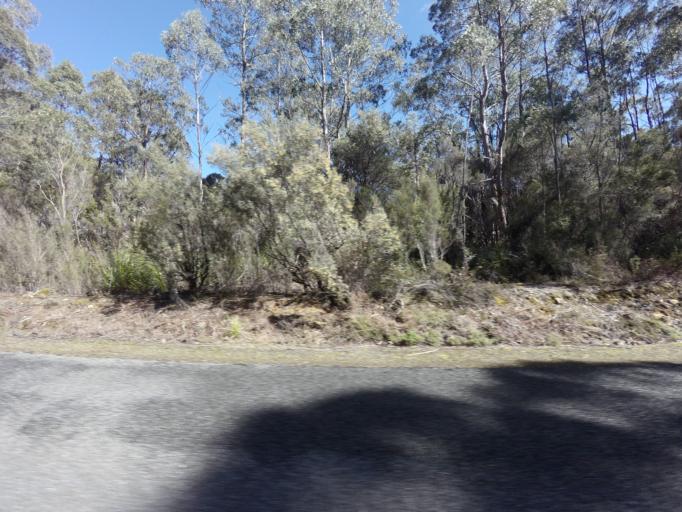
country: AU
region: Tasmania
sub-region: Derwent Valley
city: New Norfolk
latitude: -42.7415
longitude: 146.4186
